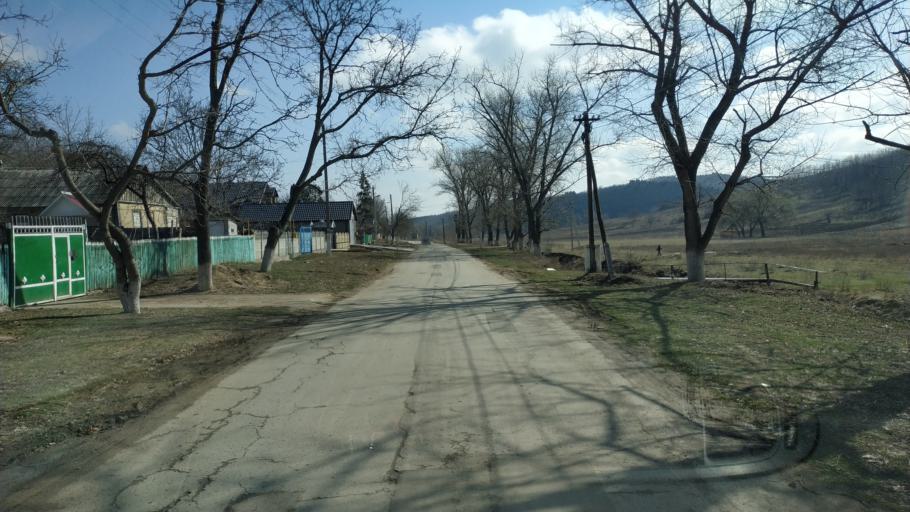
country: MD
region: Hincesti
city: Hincesti
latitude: 46.8741
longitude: 28.6313
